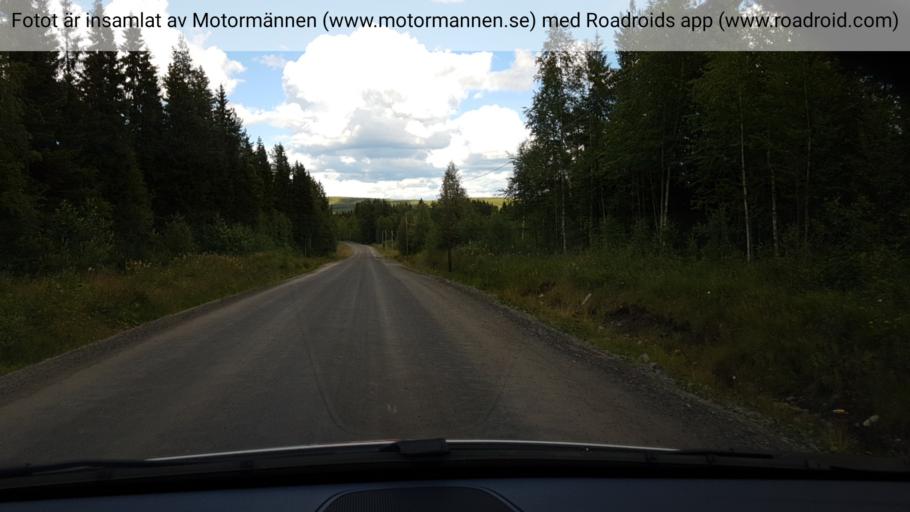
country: SE
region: Vaesternorrland
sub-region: Solleftea Kommun
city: As
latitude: 63.4542
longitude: 16.2342
